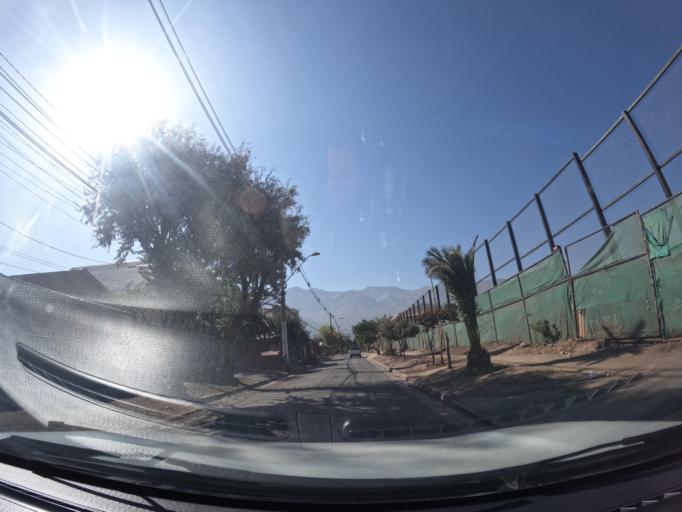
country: CL
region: Santiago Metropolitan
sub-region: Provincia de Santiago
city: Villa Presidente Frei, Nunoa, Santiago, Chile
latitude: -33.4651
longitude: -70.5583
